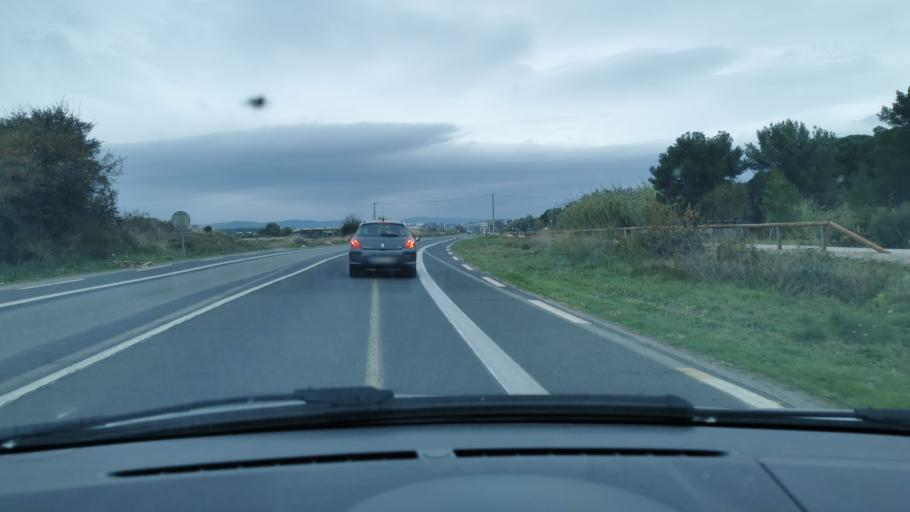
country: FR
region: Languedoc-Roussillon
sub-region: Departement de l'Herault
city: Balaruc-les-Bains
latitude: 43.4323
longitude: 3.7031
